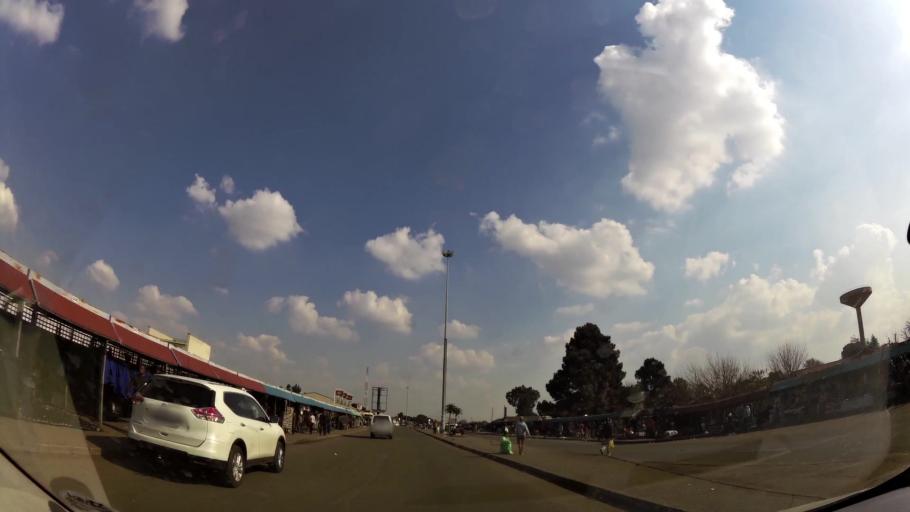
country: ZA
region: Gauteng
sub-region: Ekurhuleni Metropolitan Municipality
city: Germiston
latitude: -26.3268
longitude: 28.1451
